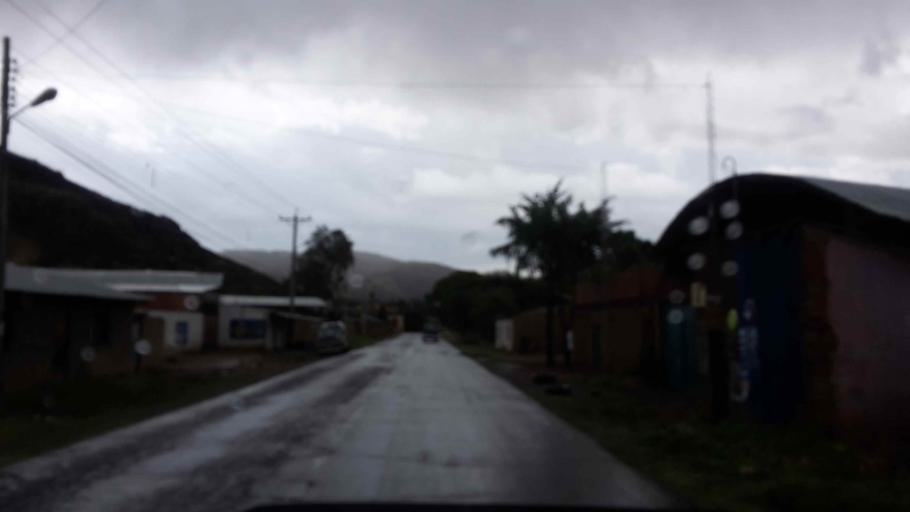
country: BO
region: Cochabamba
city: Tarata
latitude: -17.5454
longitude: -66.1032
